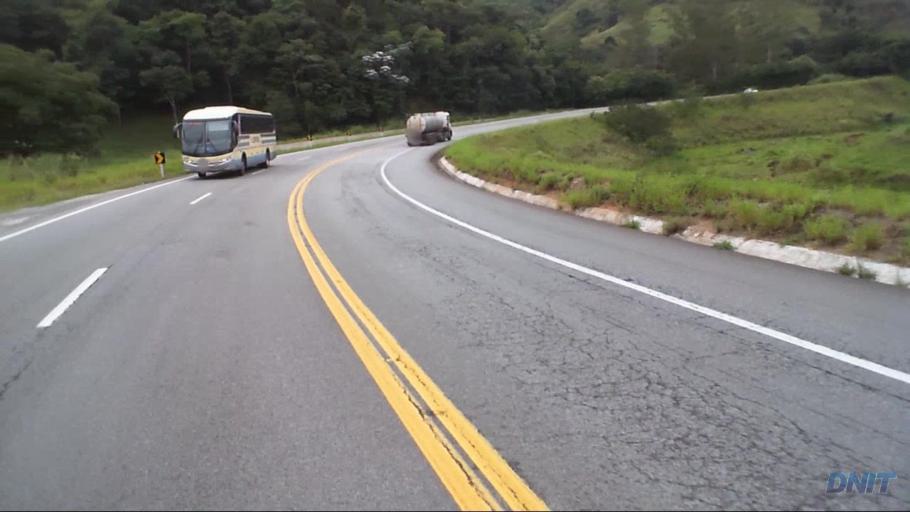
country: BR
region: Minas Gerais
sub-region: Nova Era
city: Nova Era
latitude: -19.6253
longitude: -42.8699
